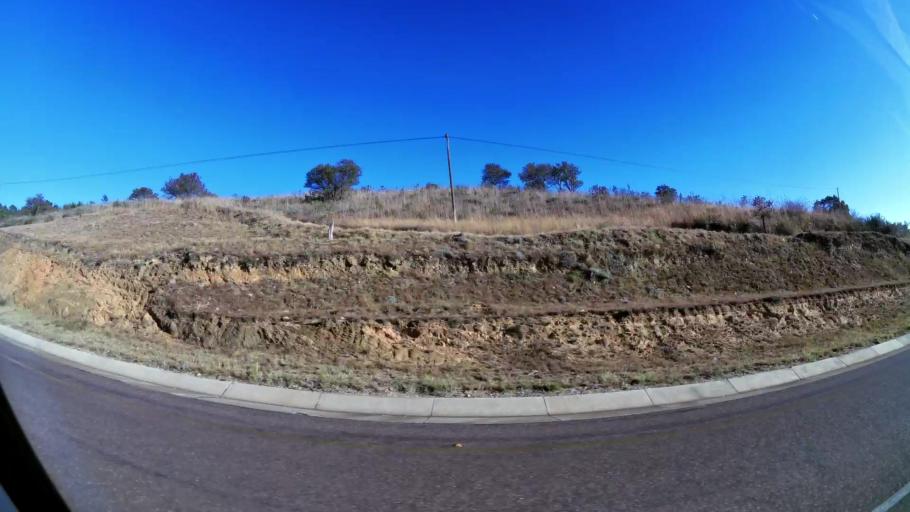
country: ZA
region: Limpopo
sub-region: Capricorn District Municipality
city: Mankoeng
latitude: -23.9321
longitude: 29.8971
